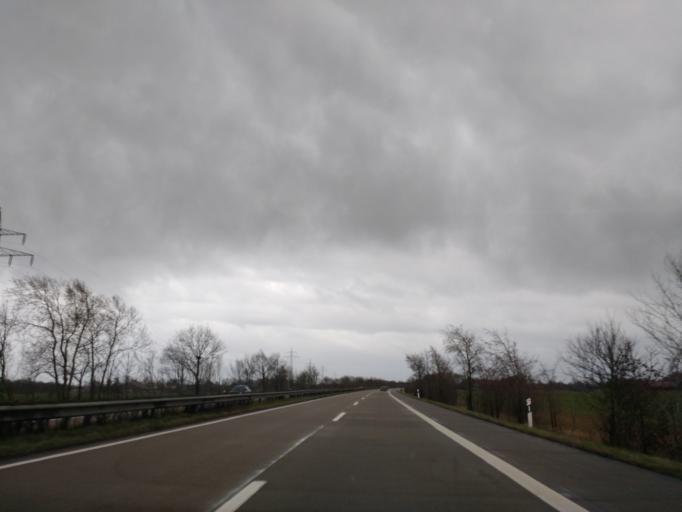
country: DE
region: Lower Saxony
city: Cuxhaven
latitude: 53.7908
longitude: 8.7083
